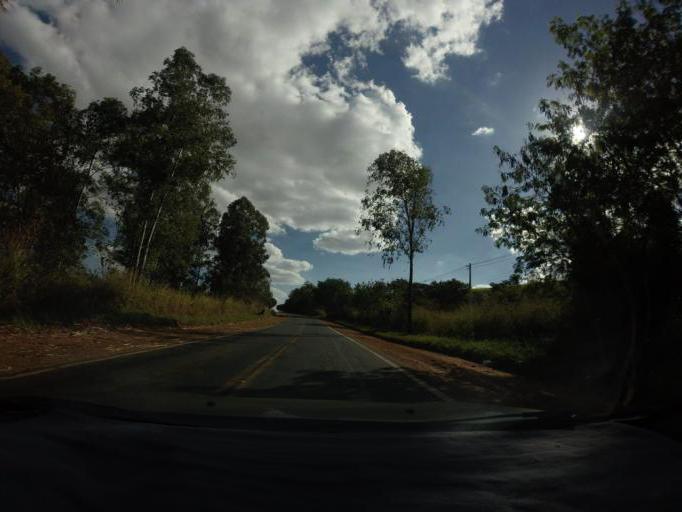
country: BR
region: Sao Paulo
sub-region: Piracicaba
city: Piracicaba
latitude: -22.7327
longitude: -47.5493
